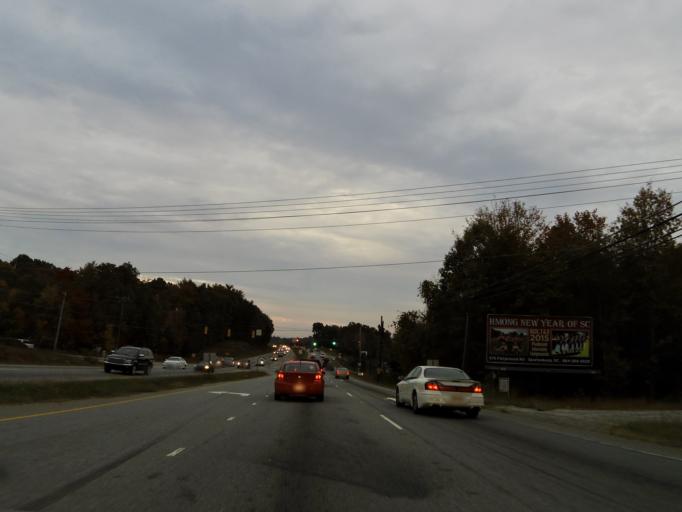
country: US
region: North Carolina
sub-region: Caldwell County
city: Northlakes
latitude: 35.7635
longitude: -81.3833
